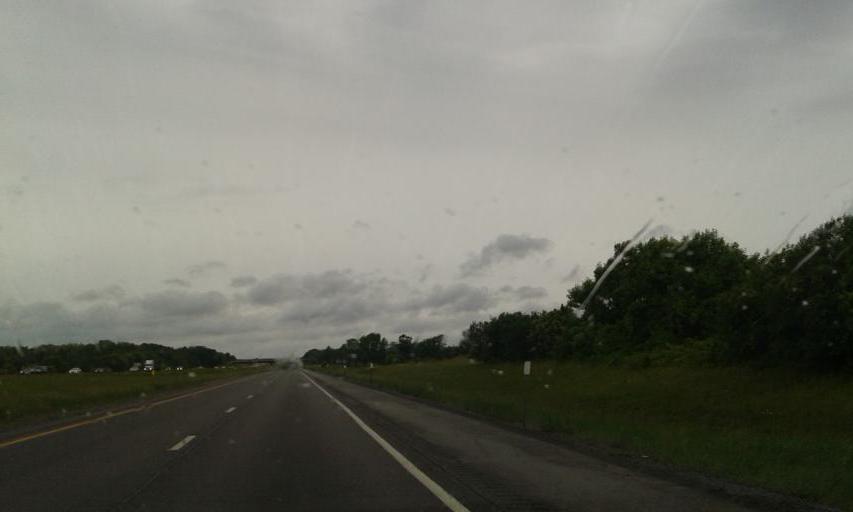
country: US
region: New York
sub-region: Genesee County
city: Batavia
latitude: 43.0182
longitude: -78.2058
